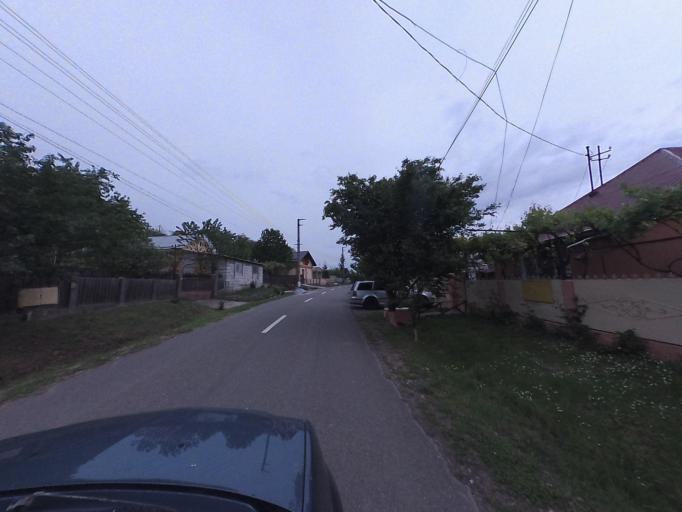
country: RO
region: Neamt
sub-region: Comuna Dulcesti
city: Dulcesti
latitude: 46.9609
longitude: 26.7927
